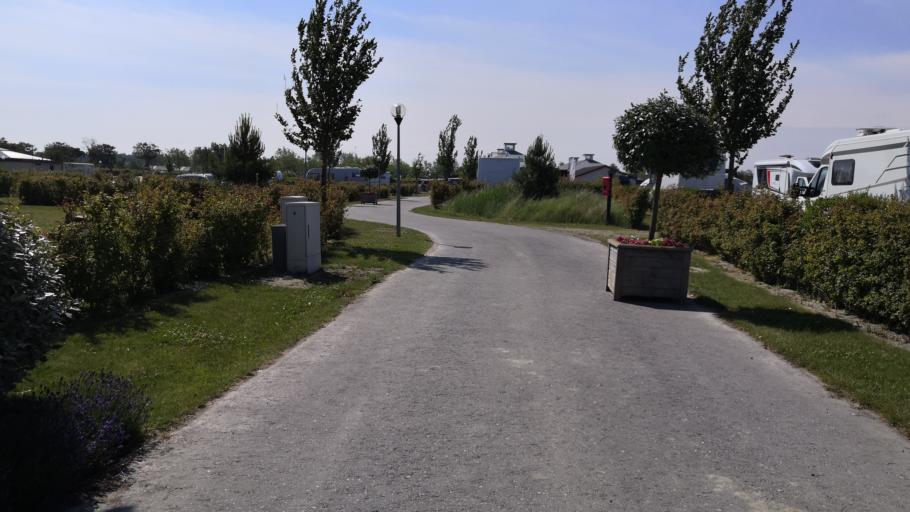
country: NL
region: Zeeland
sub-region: Gemeente Middelburg
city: Middelburg
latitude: 51.5575
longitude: 3.5151
